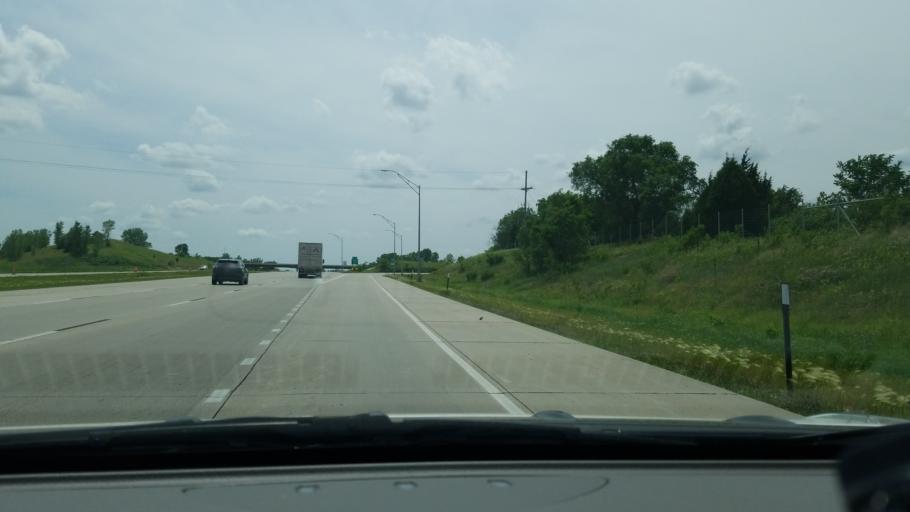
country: US
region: Nebraska
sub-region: Saunders County
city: Ashland
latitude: 41.0165
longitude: -96.3053
